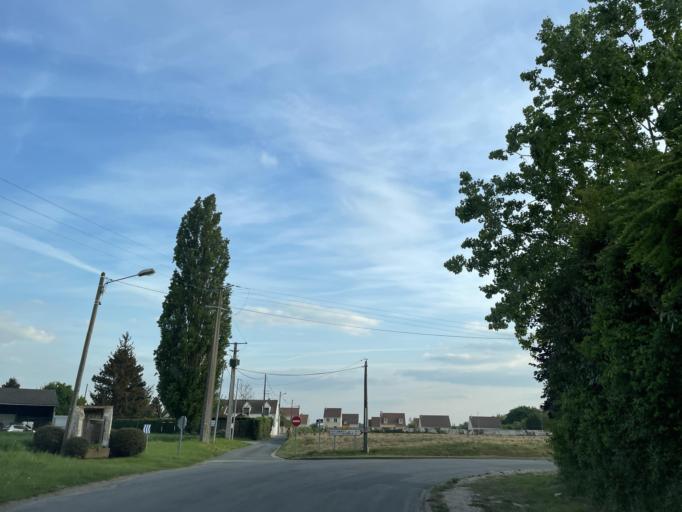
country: FR
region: Ile-de-France
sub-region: Departement de Seine-et-Marne
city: Bouleurs
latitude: 48.8913
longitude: 2.9348
